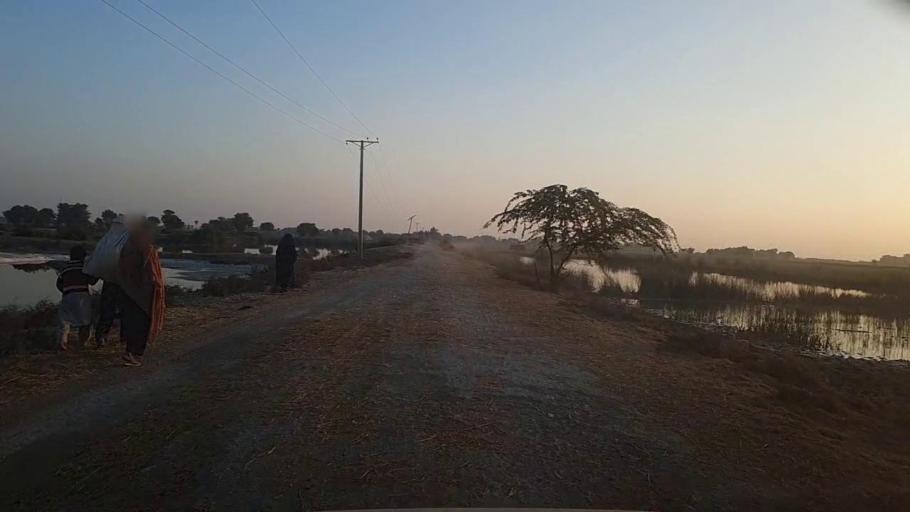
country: PK
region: Sindh
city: Khairpur Nathan Shah
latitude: 27.1648
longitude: 67.7322
